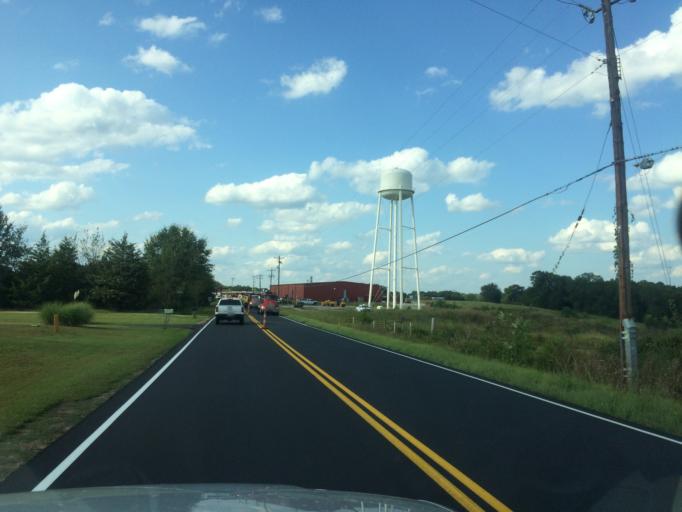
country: US
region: South Carolina
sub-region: Greenwood County
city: Ware Shoals
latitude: 34.5048
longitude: -82.1800
